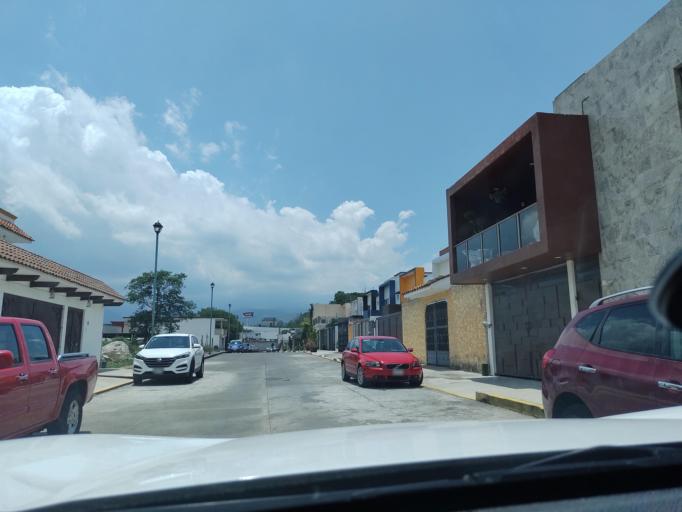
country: MX
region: Veracruz
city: Coatepec
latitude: 19.4469
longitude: -96.9494
